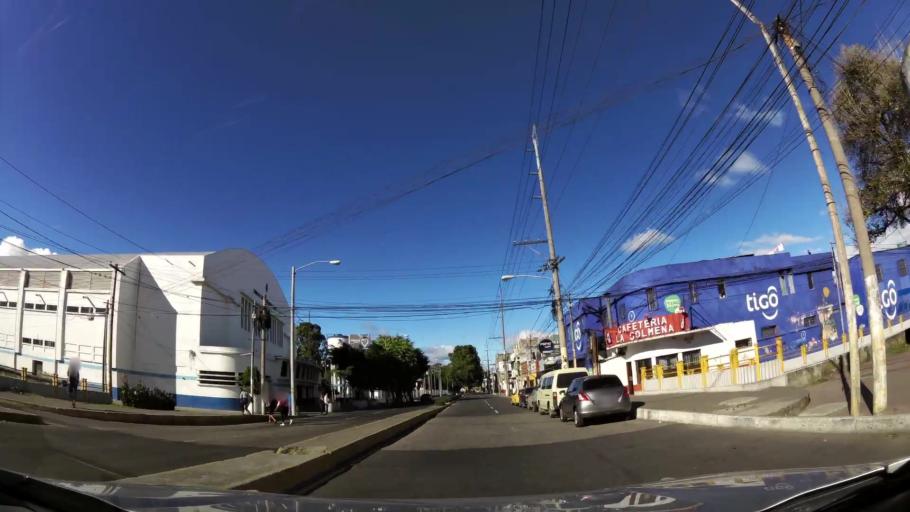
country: GT
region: Guatemala
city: Guatemala City
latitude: 14.6228
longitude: -90.5095
